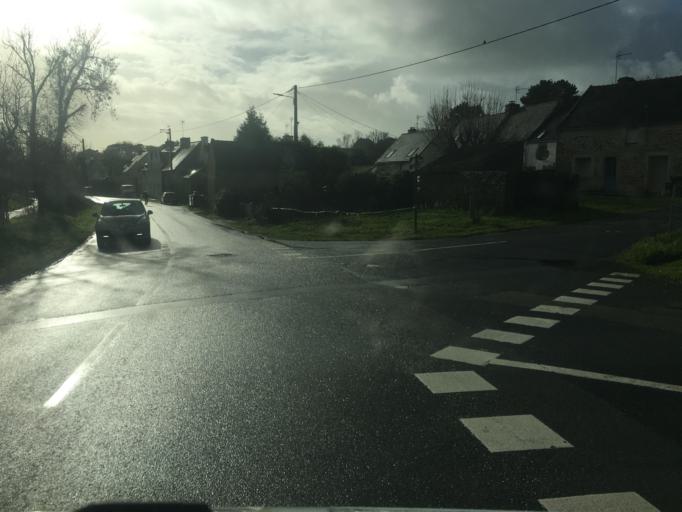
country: FR
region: Brittany
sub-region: Departement du Morbihan
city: Sarzeau
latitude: 47.5049
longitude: -2.7726
